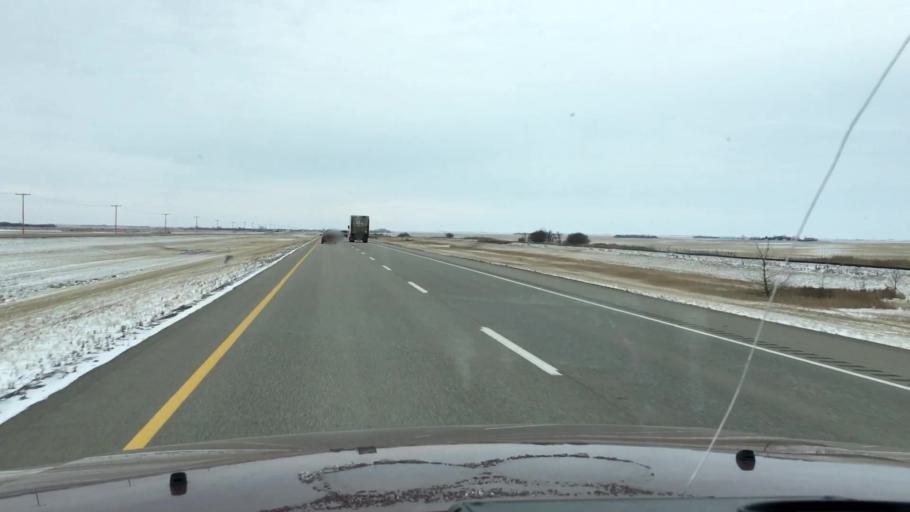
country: CA
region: Saskatchewan
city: Watrous
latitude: 51.1891
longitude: -105.9471
